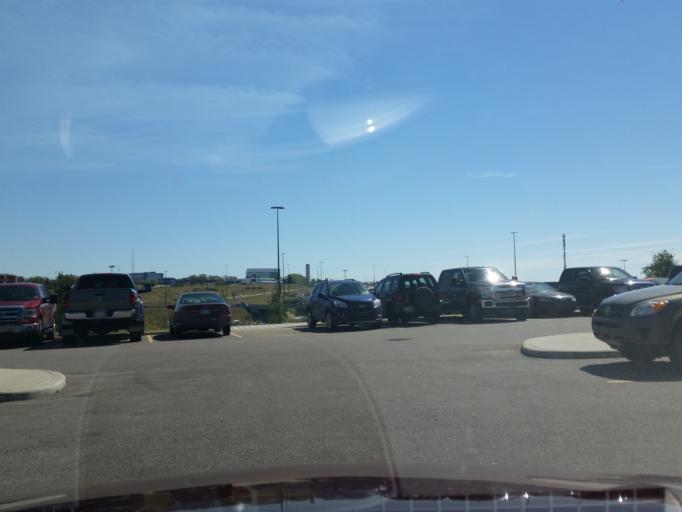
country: CA
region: Alberta
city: Calgary
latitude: 51.0497
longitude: -114.0250
